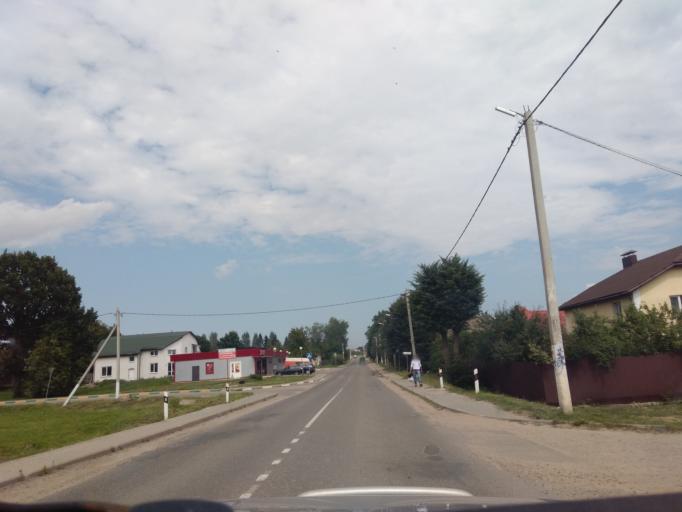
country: BY
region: Minsk
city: Khatsyezhyna
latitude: 53.9107
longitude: 27.3090
